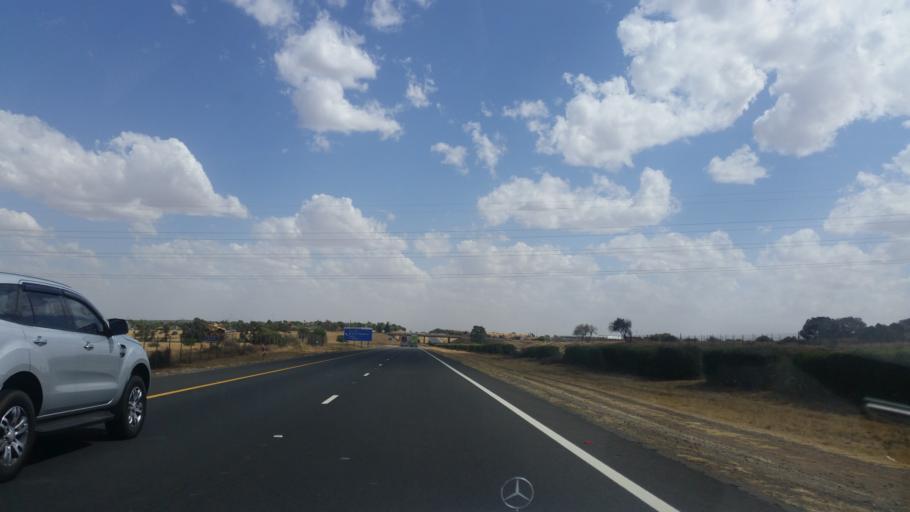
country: ZA
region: Orange Free State
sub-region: Mangaung Metropolitan Municipality
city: Bloemfontein
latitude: -29.0852
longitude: 26.1749
